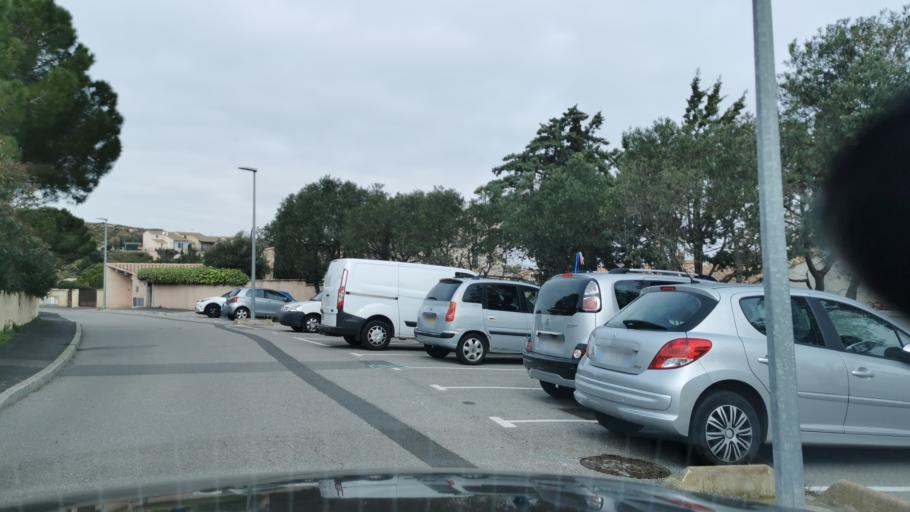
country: FR
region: Languedoc-Roussillon
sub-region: Departement de l'Aude
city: Narbonne
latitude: 43.1653
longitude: 2.9786
